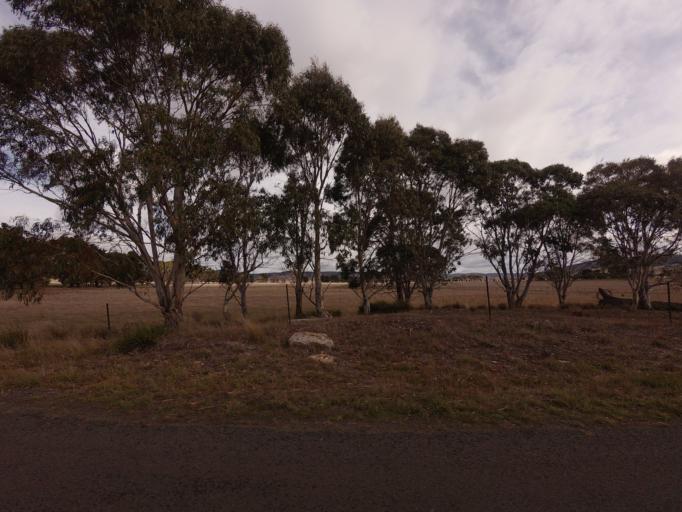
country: AU
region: Tasmania
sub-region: Brighton
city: Bridgewater
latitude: -42.4078
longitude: 147.3967
